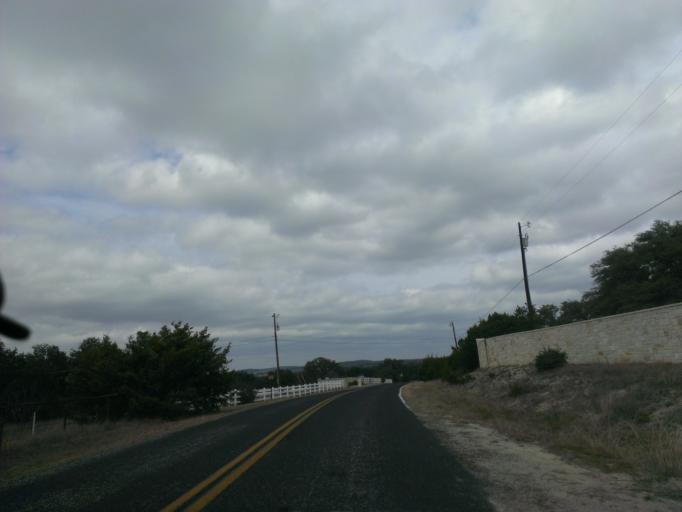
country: US
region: Texas
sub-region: Travis County
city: Briarcliff
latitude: 30.3899
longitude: -98.1037
